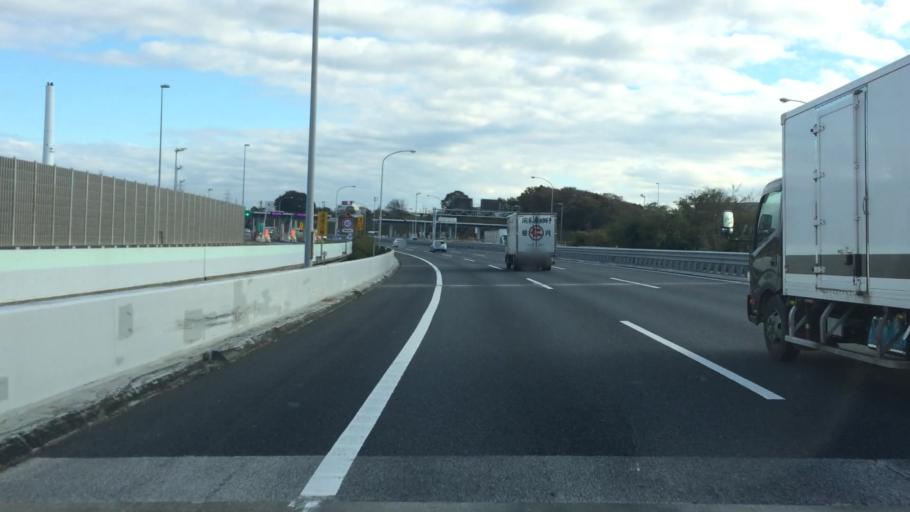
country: JP
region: Chiba
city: Yotsukaido
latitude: 35.6653
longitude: 140.1091
